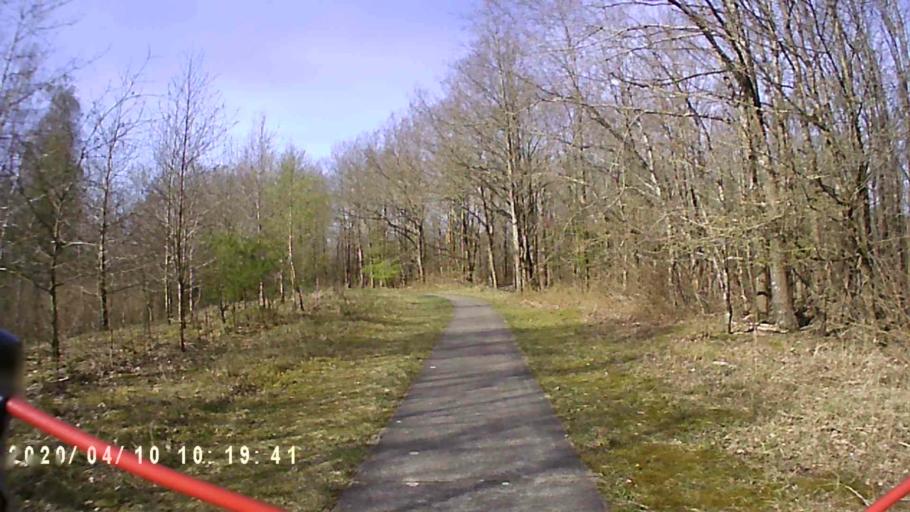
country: NL
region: Friesland
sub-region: Gemeente Dongeradeel
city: Anjum
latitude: 53.3802
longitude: 6.2232
